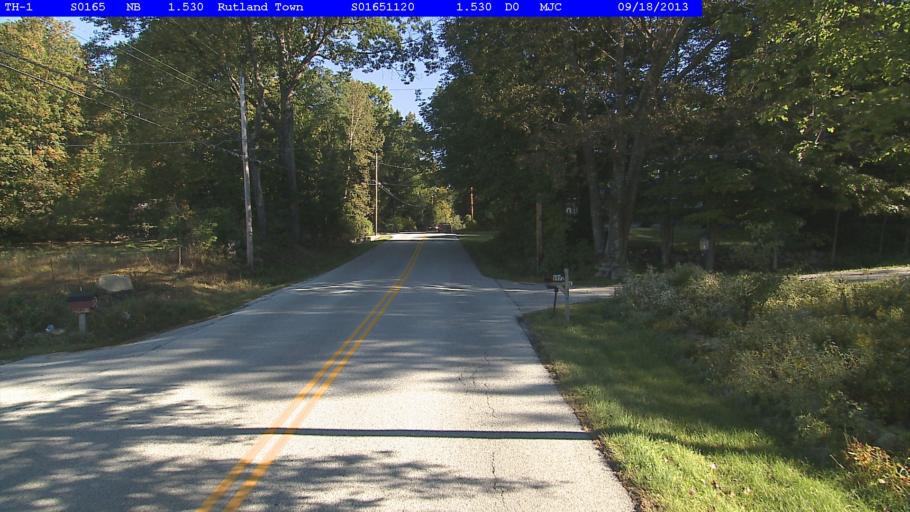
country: US
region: Vermont
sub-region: Rutland County
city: Rutland
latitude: 43.6617
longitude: -72.9500
